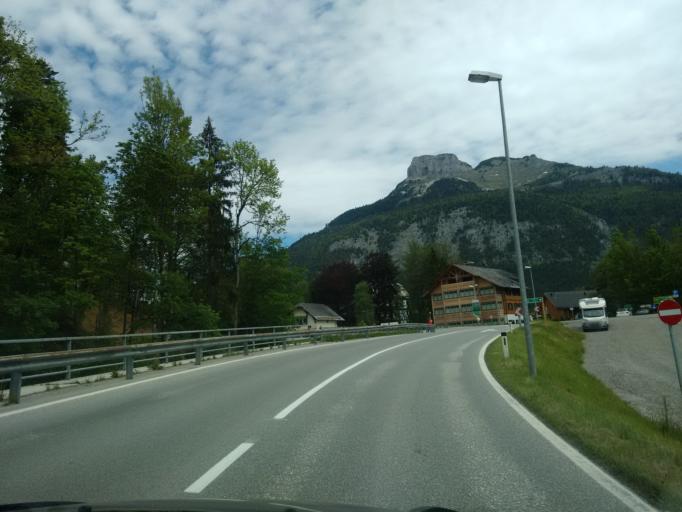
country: AT
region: Styria
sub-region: Politischer Bezirk Liezen
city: Altaussee
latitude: 47.6321
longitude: 13.7641
